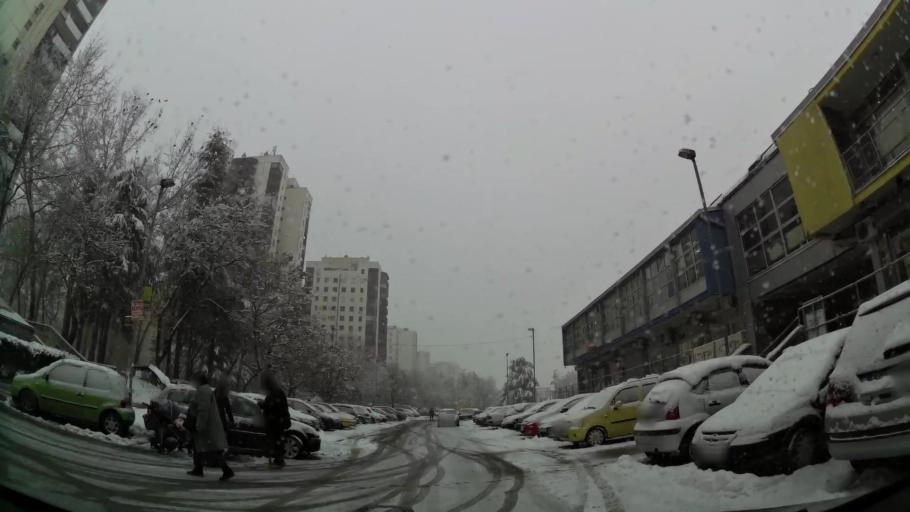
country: RS
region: Central Serbia
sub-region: Belgrade
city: Zemun
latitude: 44.8073
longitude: 20.3825
